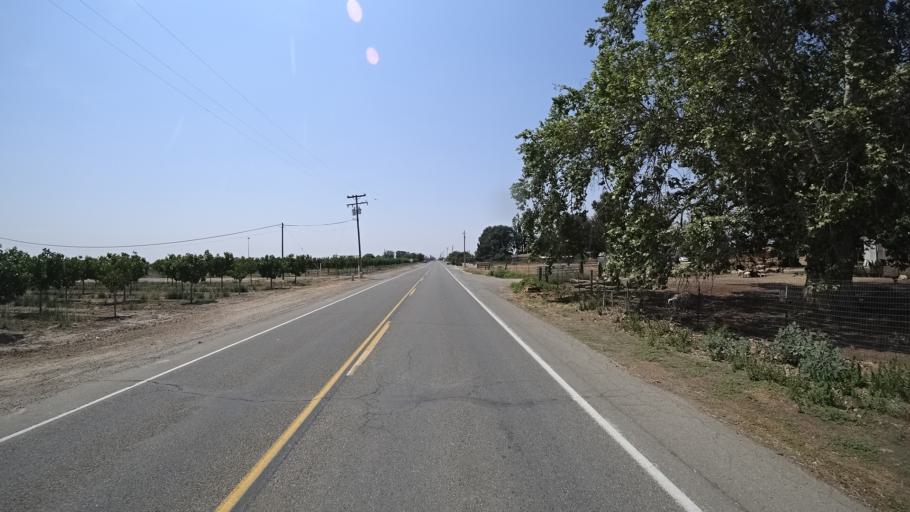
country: US
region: California
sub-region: Kings County
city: Lemoore
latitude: 36.3415
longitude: -119.7809
